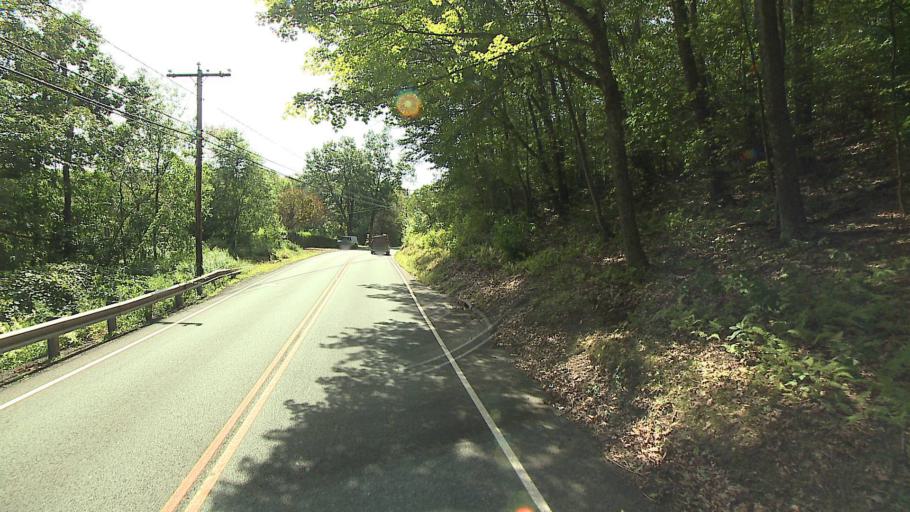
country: US
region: Connecticut
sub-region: Litchfield County
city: Plymouth
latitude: 41.6644
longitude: -73.0491
